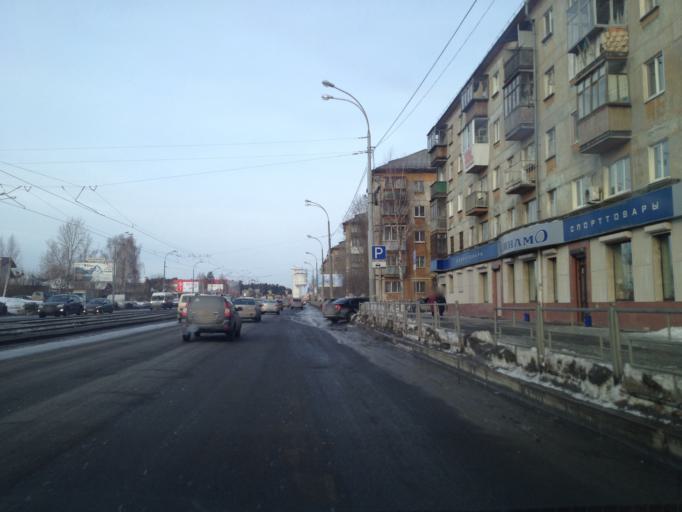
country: RU
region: Sverdlovsk
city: Yekaterinburg
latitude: 56.8882
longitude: 60.5670
